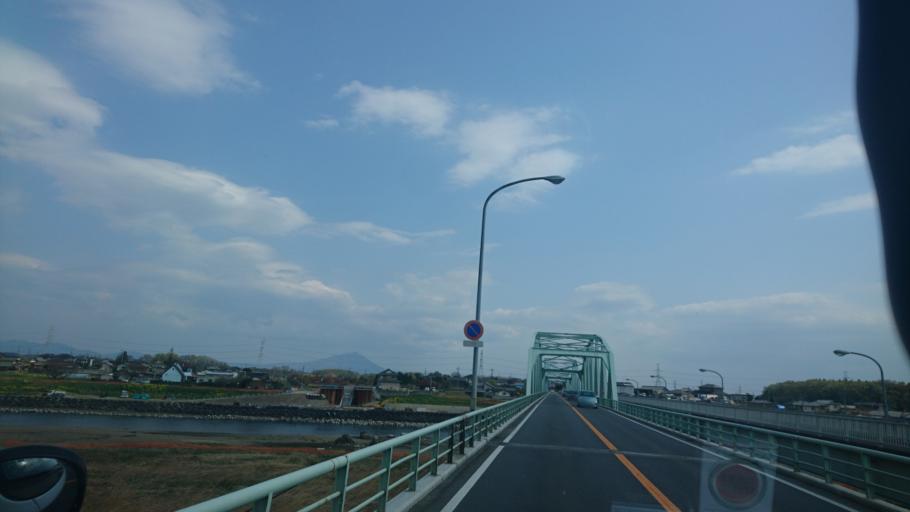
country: JP
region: Ibaraki
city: Yuki
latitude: 36.2782
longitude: 139.9054
